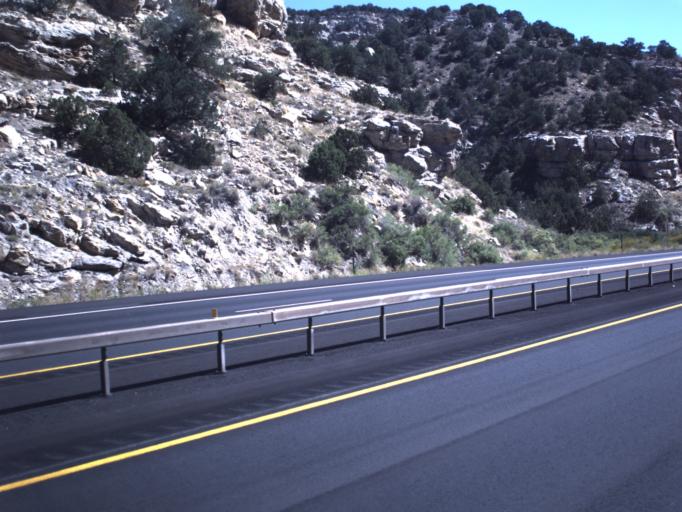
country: US
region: Utah
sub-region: Sevier County
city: Salina
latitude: 38.9061
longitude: -111.6925
